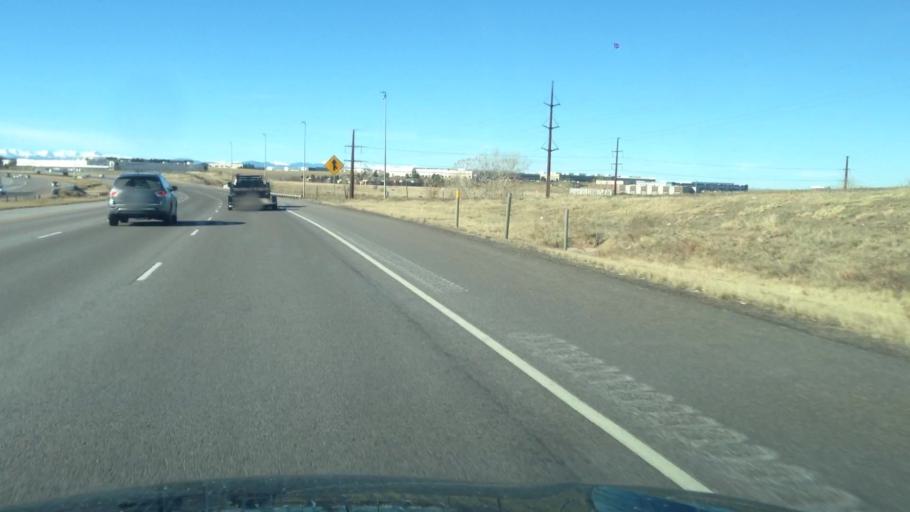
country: US
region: Colorado
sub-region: Douglas County
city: Stonegate
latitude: 39.5540
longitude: -104.8095
